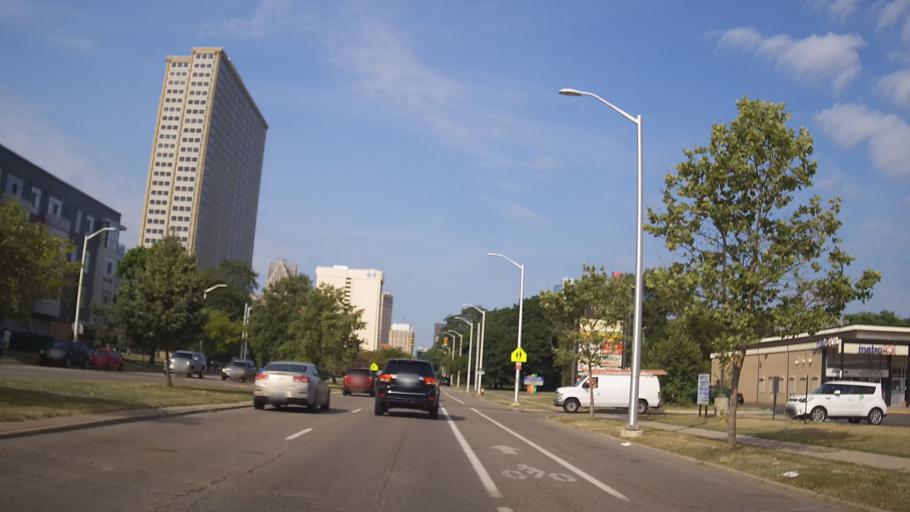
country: US
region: Michigan
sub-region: Wayne County
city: Detroit
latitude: 42.3384
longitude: -83.0319
